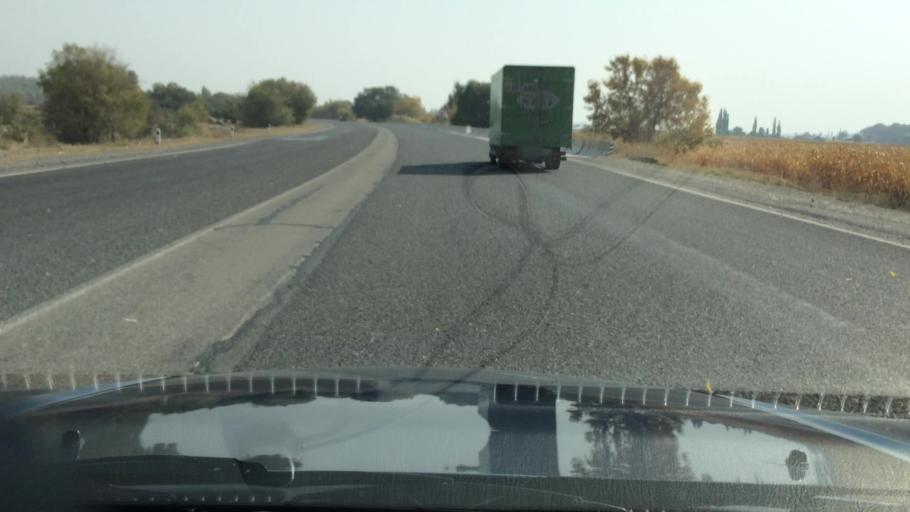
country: KG
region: Chuy
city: Ivanovka
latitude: 42.9409
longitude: 74.9688
